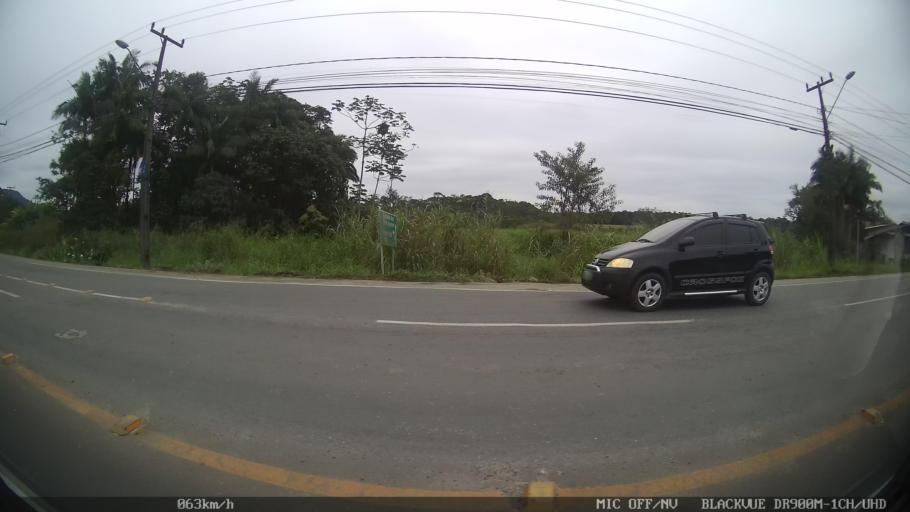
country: BR
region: Santa Catarina
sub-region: Joinville
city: Joinville
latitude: -26.2829
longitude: -48.9229
